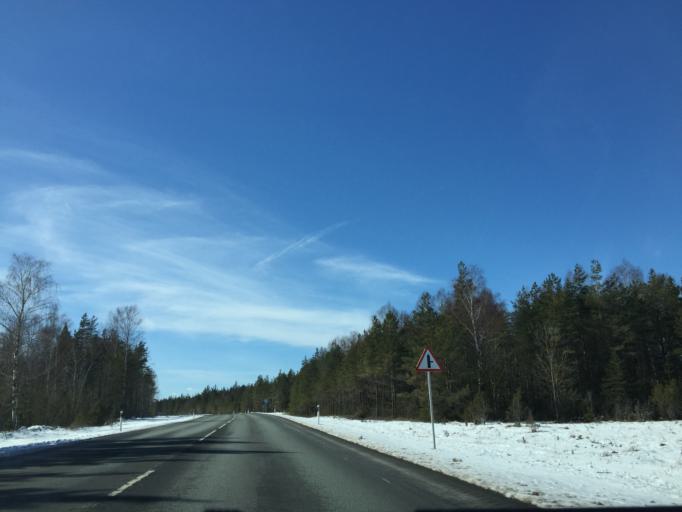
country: EE
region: Laeaene
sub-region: Lihula vald
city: Lihula
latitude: 58.6098
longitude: 23.5722
